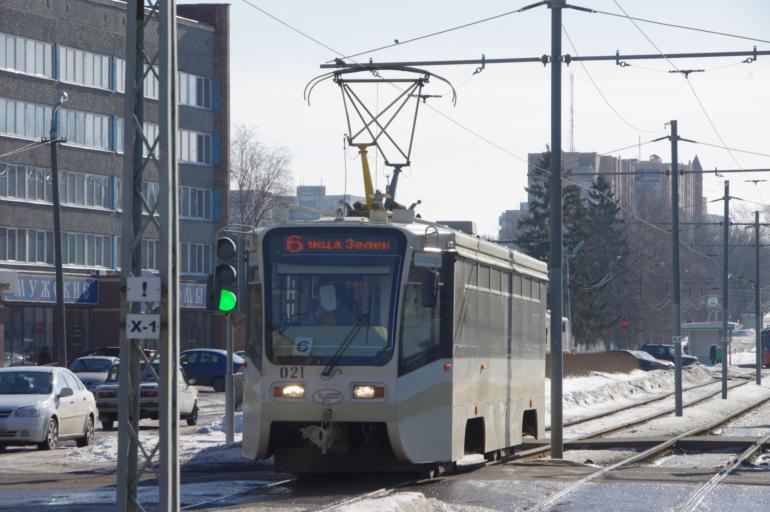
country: RU
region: Moskovskaya
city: Kolomna
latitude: 55.0922
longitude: 38.7679
